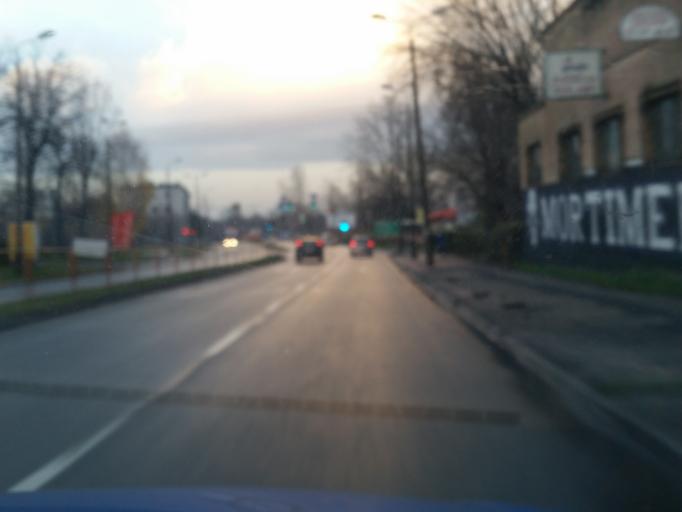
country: PL
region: Silesian Voivodeship
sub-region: Dabrowa Gornicza
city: Dabrowa Gornicza
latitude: 50.3131
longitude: 19.1950
